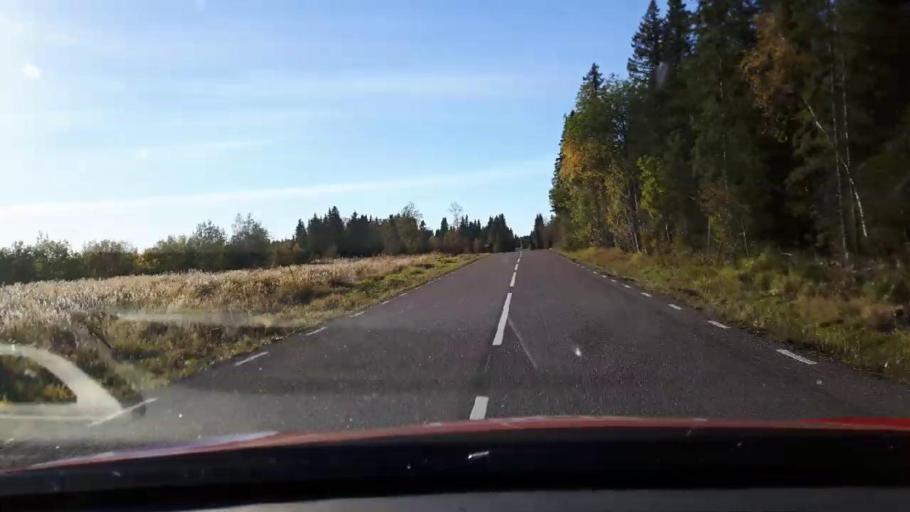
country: SE
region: Jaemtland
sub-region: Stroemsunds Kommun
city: Stroemsund
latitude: 63.8635
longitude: 15.1566
